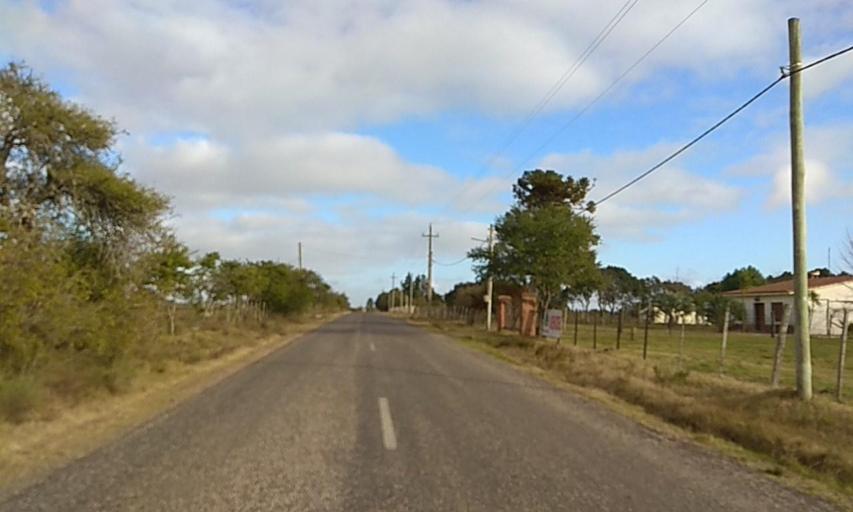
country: UY
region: Florida
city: Florida
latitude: -34.0533
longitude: -56.1966
